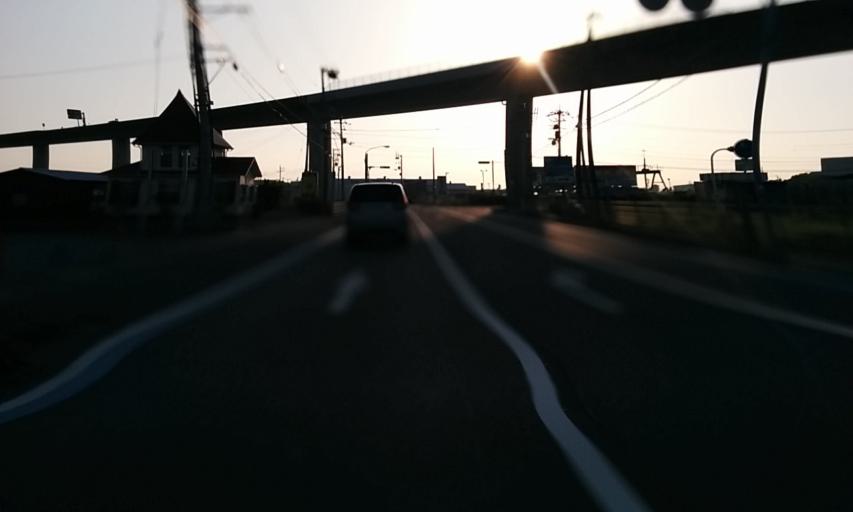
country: JP
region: Ehime
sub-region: Shikoku-chuo Shi
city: Matsuyama
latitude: 33.7897
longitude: 132.7729
